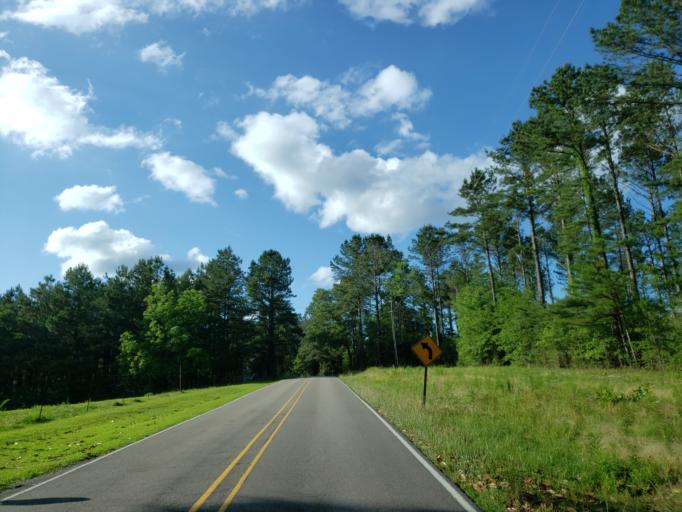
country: US
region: Mississippi
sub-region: Forrest County
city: Petal
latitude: 31.3252
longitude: -89.2118
